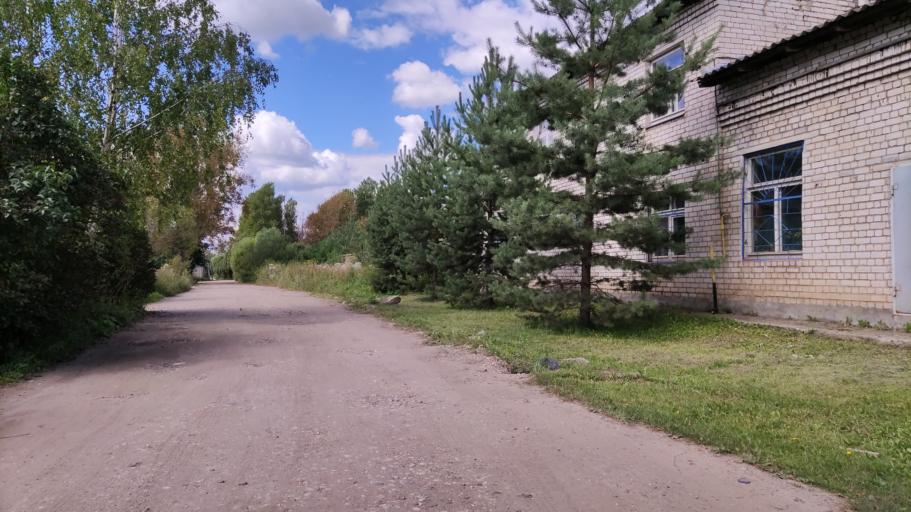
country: RU
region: Tverskaya
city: Rzhev
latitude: 56.2381
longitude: 34.3222
